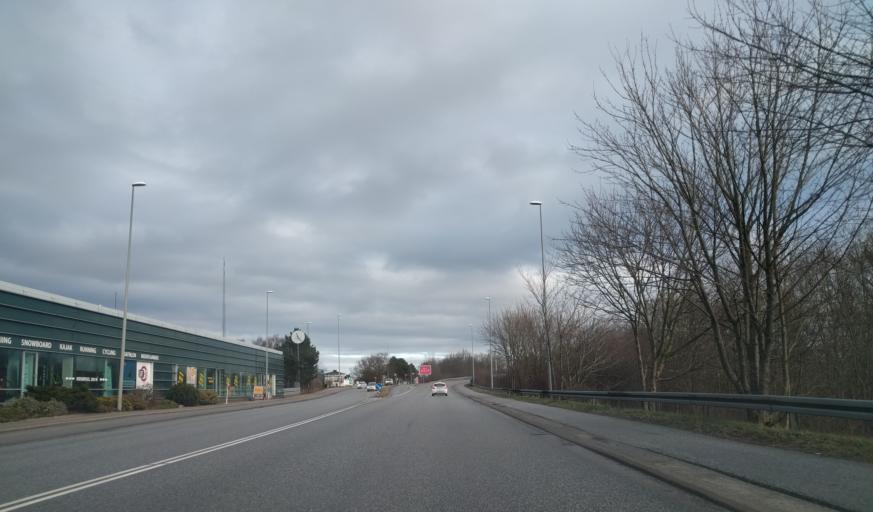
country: DK
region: North Denmark
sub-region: Alborg Kommune
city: Aalborg
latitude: 57.0175
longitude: 9.8965
